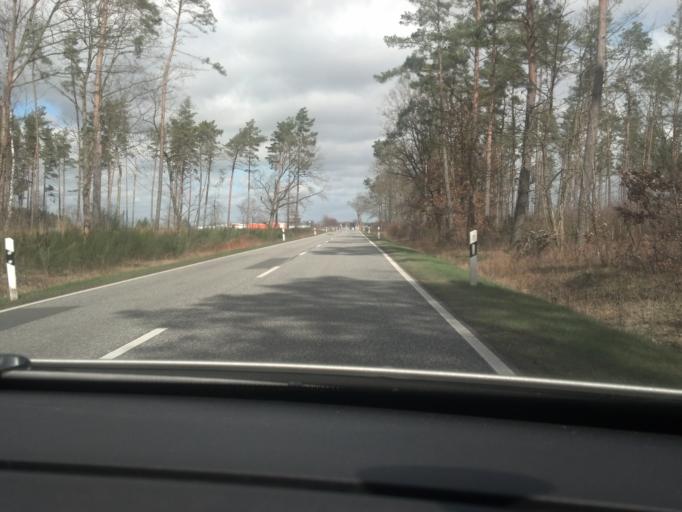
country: DE
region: Mecklenburg-Vorpommern
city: Plau am See
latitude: 53.3670
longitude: 12.2473
